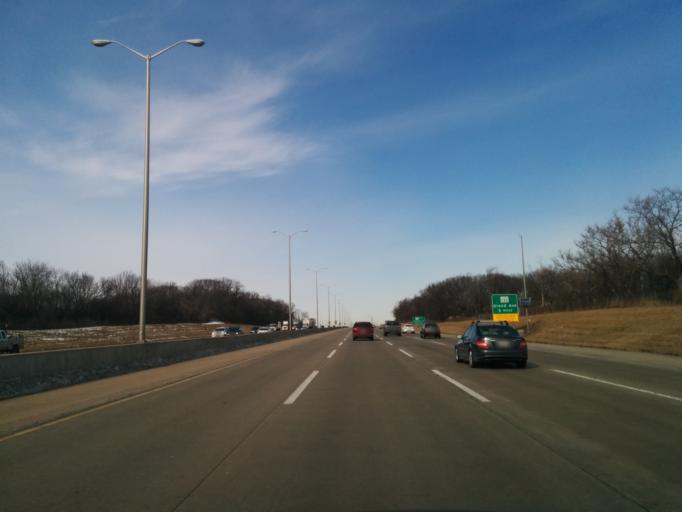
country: US
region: Illinois
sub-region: Lake County
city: Park City
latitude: 42.3366
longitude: -87.9151
